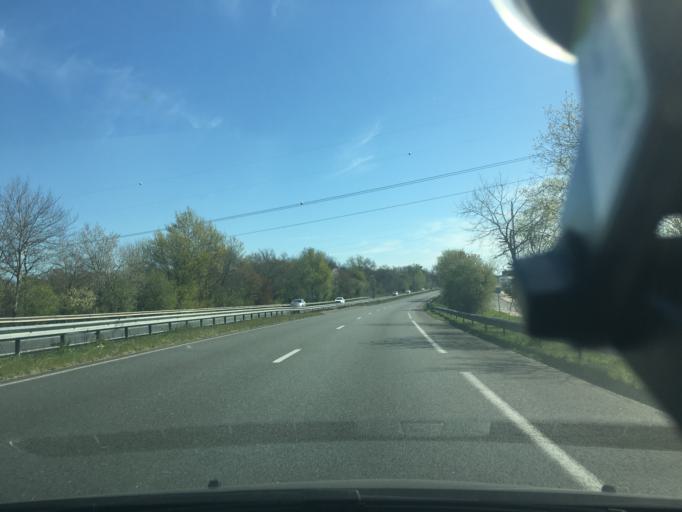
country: FR
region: Aquitaine
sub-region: Departement de la Gironde
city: Yvrac
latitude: 44.8696
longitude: -0.4649
